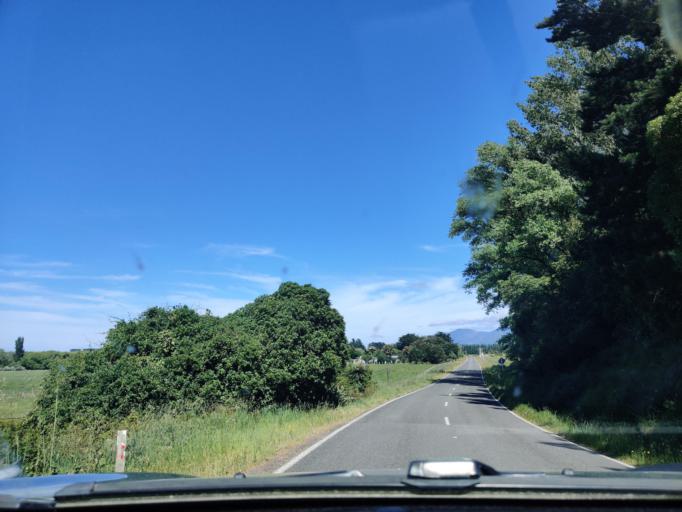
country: NZ
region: Wellington
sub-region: Upper Hutt City
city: Upper Hutt
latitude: -41.3665
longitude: 175.1955
